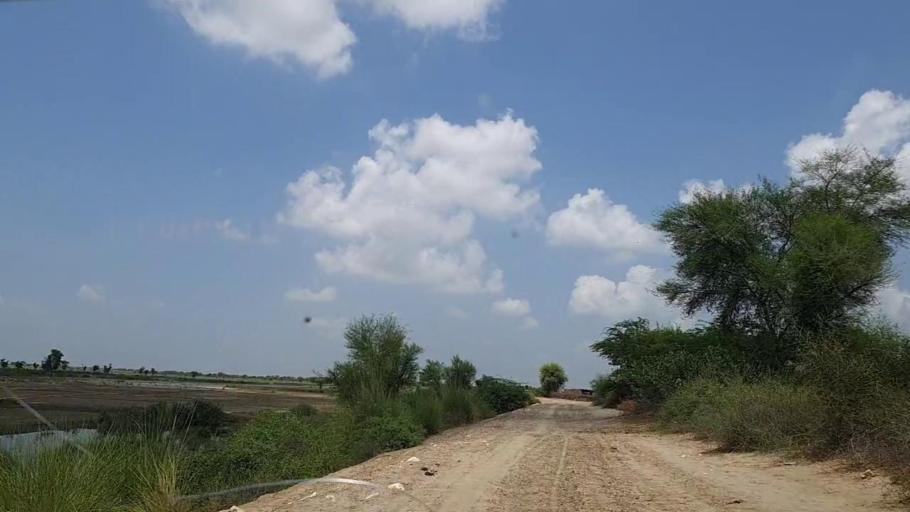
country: PK
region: Sindh
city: Tharu Shah
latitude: 26.9638
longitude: 68.0305
